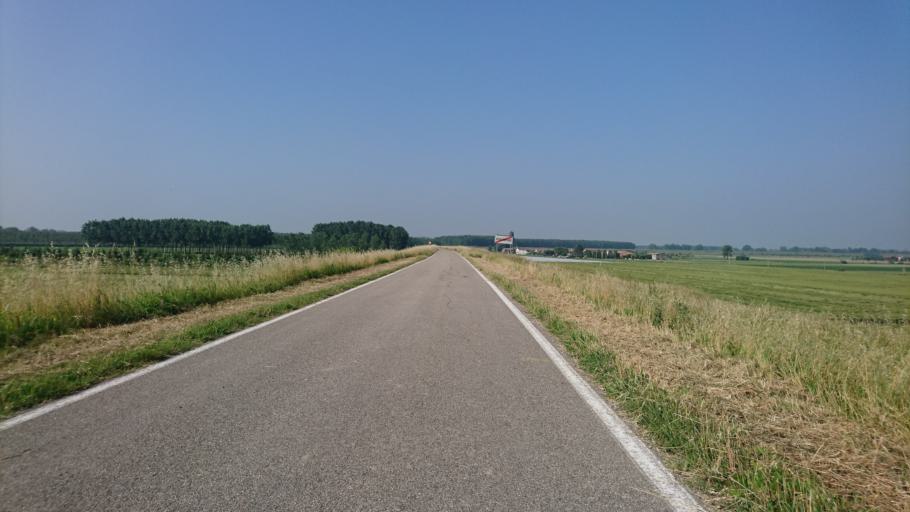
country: IT
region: Veneto
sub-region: Provincia di Rovigo
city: Bergantino
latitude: 45.0551
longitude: 11.2481
